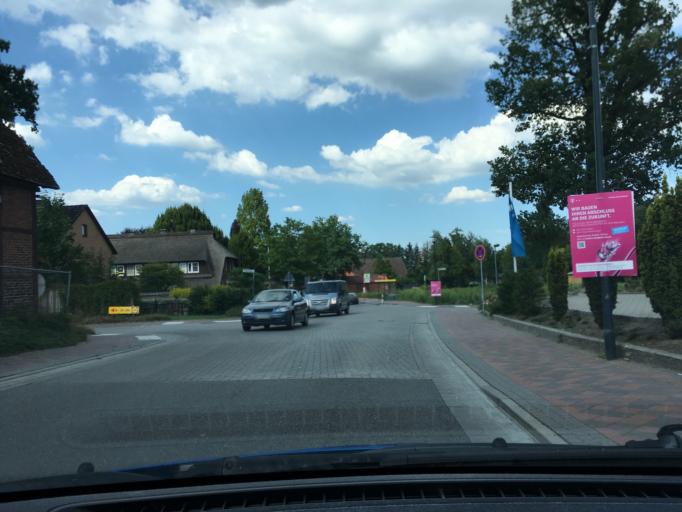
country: DE
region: Lower Saxony
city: Harmstorf
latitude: 53.3915
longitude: 10.0366
